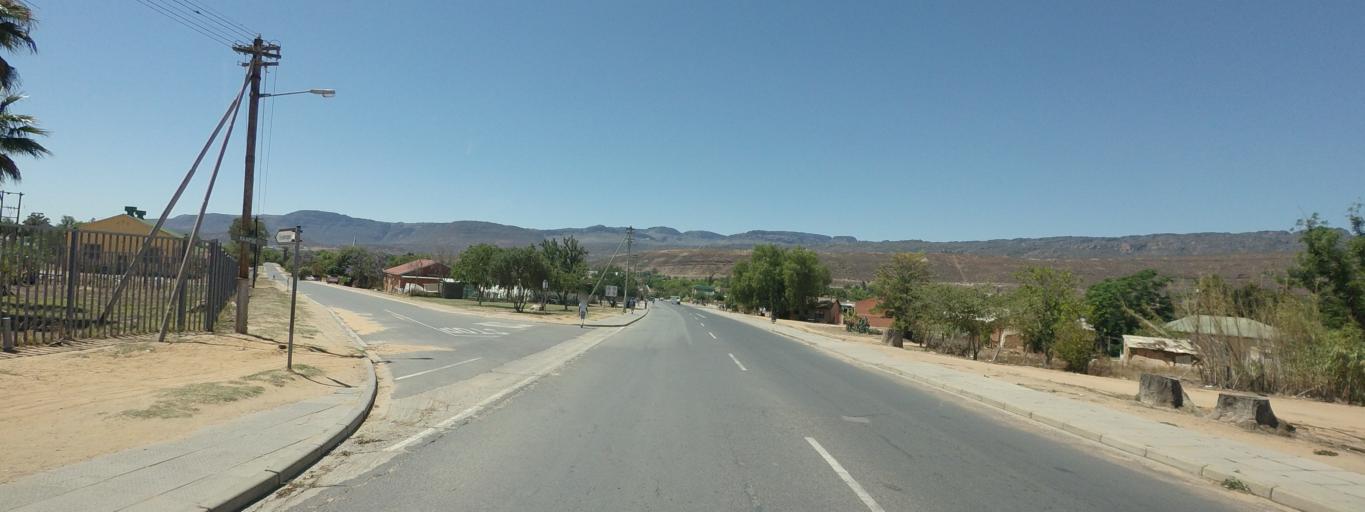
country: ZA
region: Western Cape
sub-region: West Coast District Municipality
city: Clanwilliam
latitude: -32.1839
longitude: 18.8921
